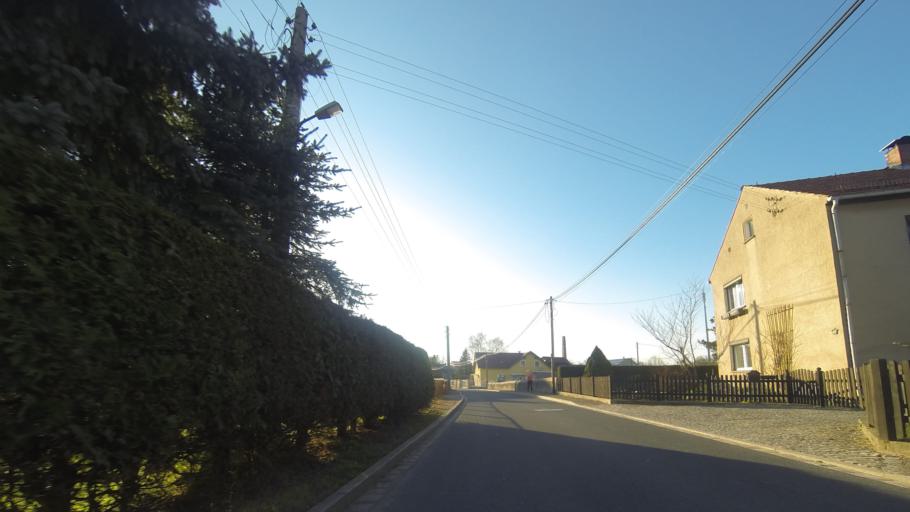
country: DE
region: Saxony
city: Ottendorf-Okrilla
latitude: 51.1627
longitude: 13.7717
